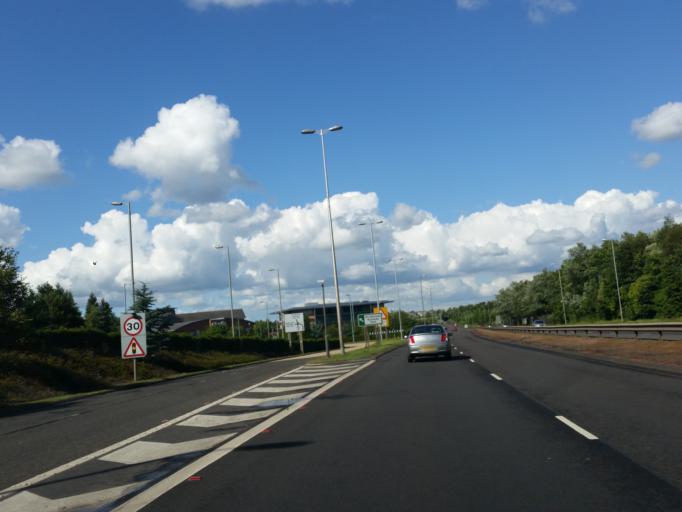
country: GB
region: Scotland
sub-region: North Lanarkshire
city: Bellshill
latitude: 55.8289
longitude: -4.0344
